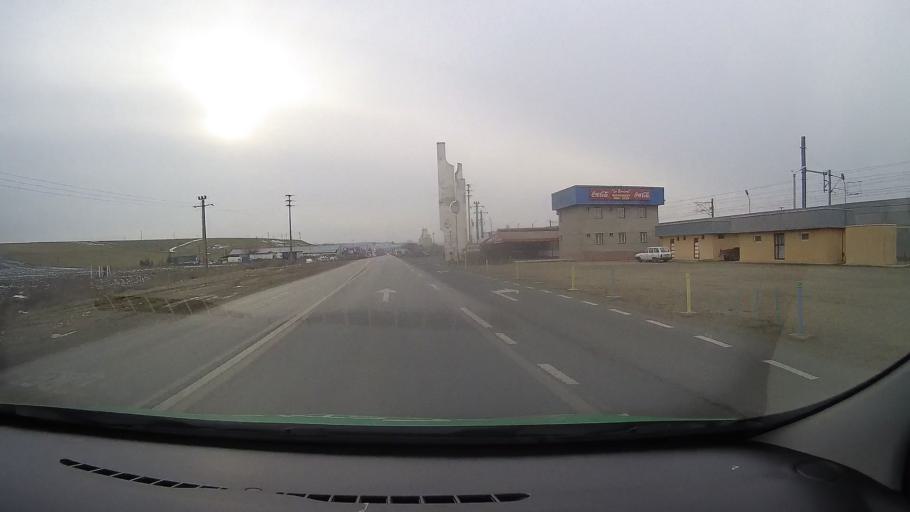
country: RO
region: Hunedoara
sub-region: Municipiul Orastie
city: Orastie
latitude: 45.8651
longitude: 23.2217
